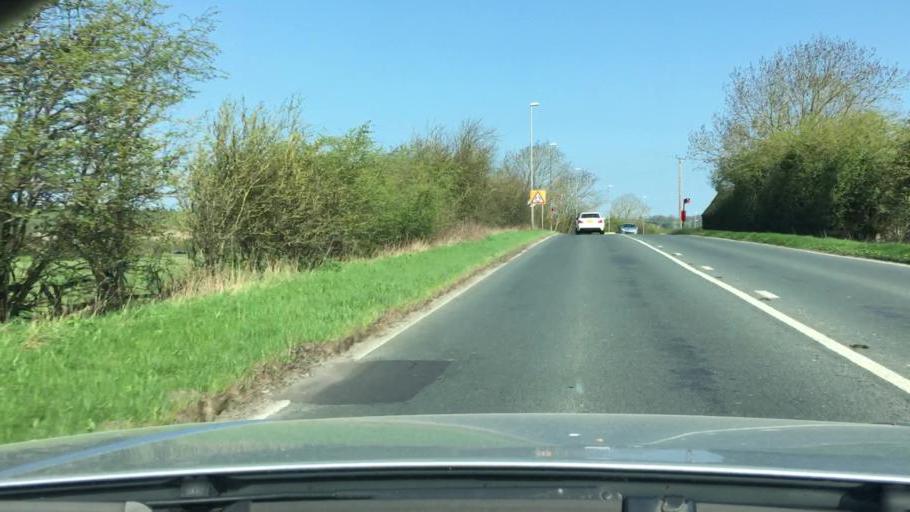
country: GB
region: England
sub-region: North Yorkshire
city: Pannal
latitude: 53.9451
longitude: -1.5399
